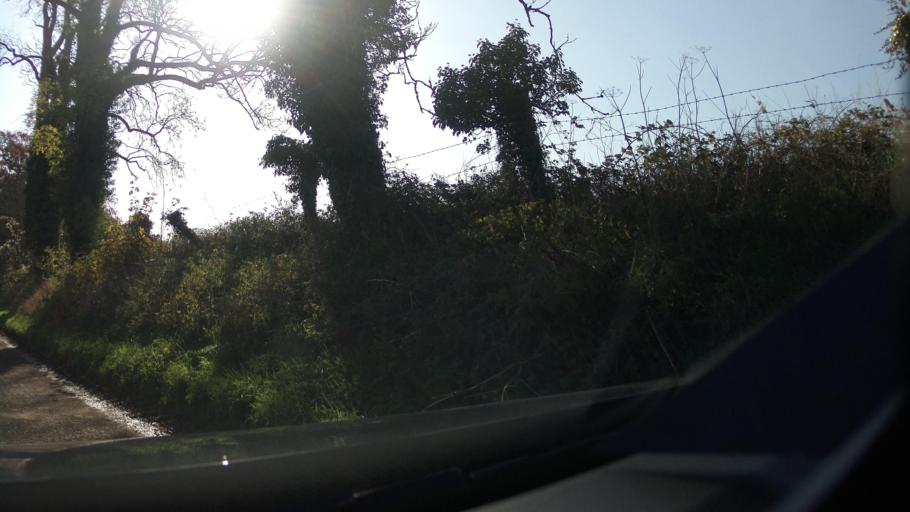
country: GB
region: England
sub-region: Somerset
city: Castle Cary
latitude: 51.0516
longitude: -2.4824
